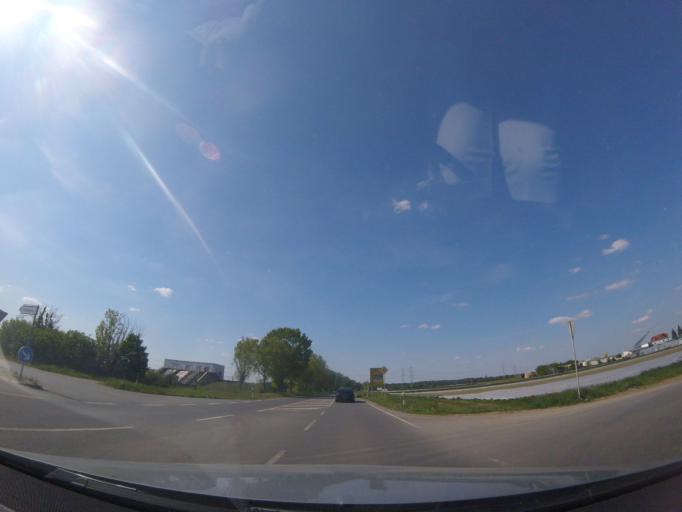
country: DE
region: Hesse
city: Griesheim
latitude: 49.8638
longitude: 8.5445
